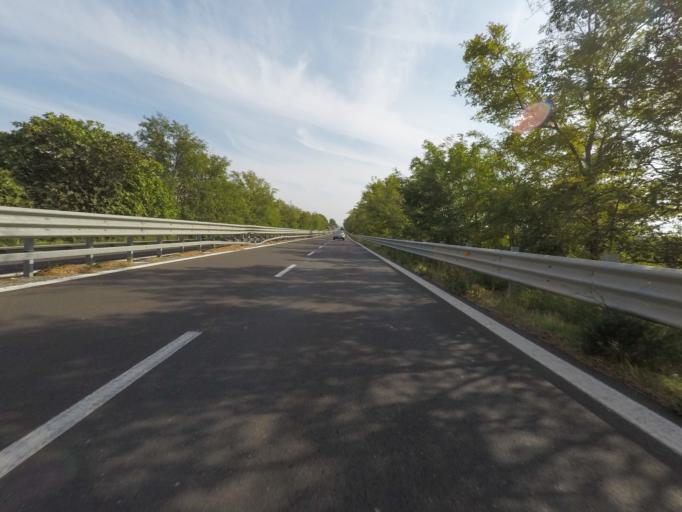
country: IT
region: Latium
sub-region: Provincia di Viterbo
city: Montalto di Castro
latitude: 42.3369
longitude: 11.6216
